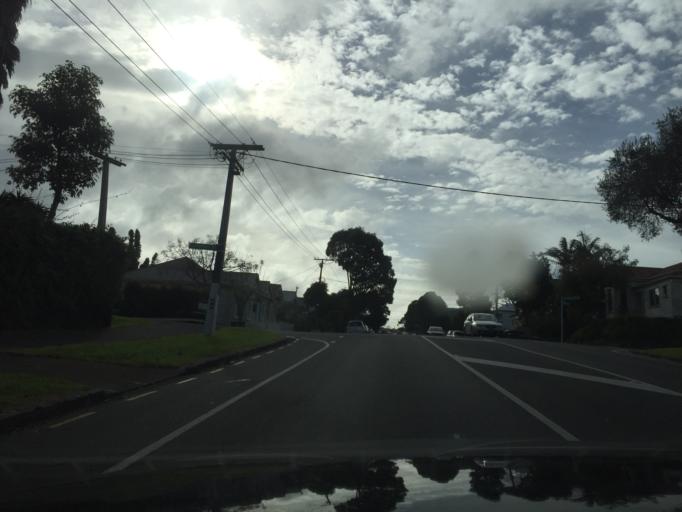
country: NZ
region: Auckland
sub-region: Auckland
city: Auckland
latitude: -36.8609
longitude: 174.7443
